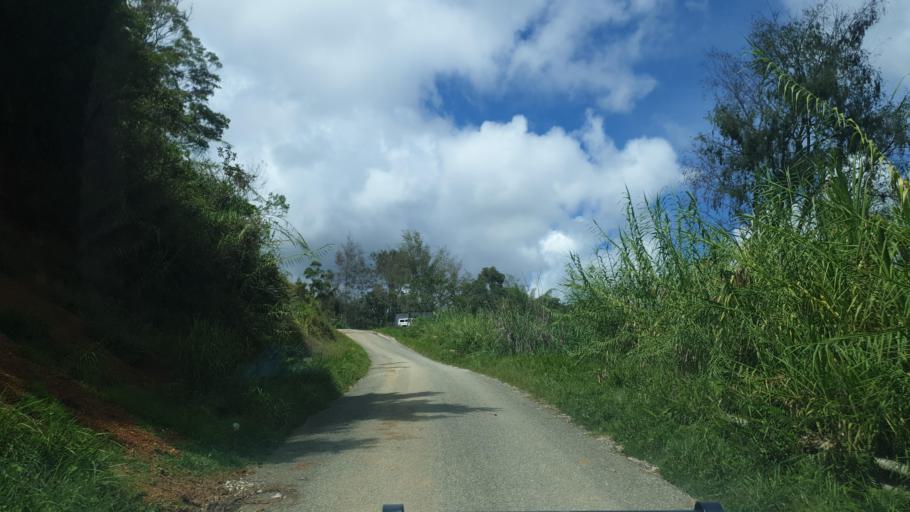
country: PG
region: Chimbu
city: Kundiawa
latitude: -6.1614
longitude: 145.1333
